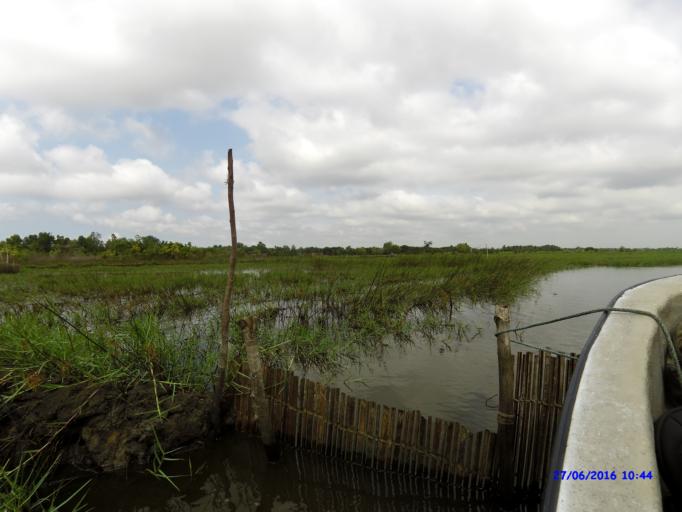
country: BJ
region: Mono
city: Come
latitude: 6.3671
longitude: 1.9244
